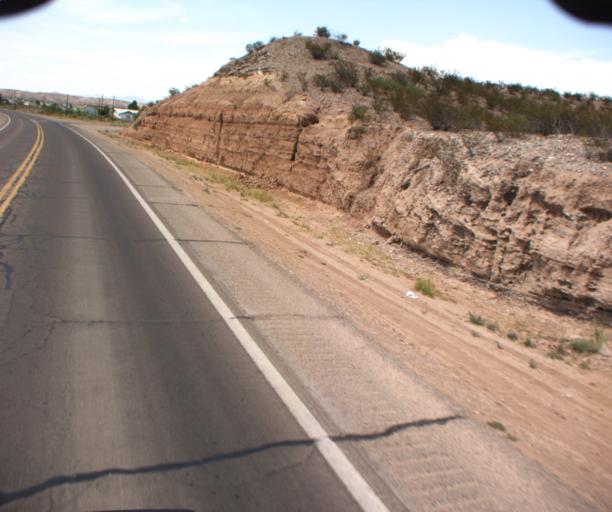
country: US
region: Arizona
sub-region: Greenlee County
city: Clifton
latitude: 32.7335
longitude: -109.0924
